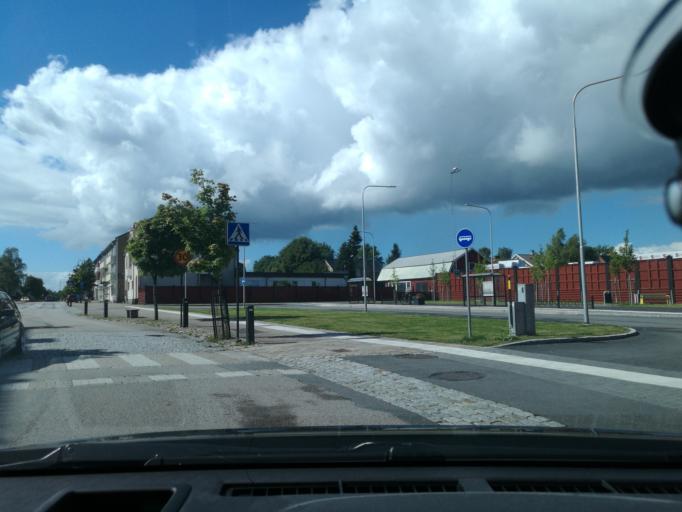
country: SE
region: Kronoberg
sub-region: Alvesta Kommun
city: Vislanda
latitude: 56.7864
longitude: 14.4534
